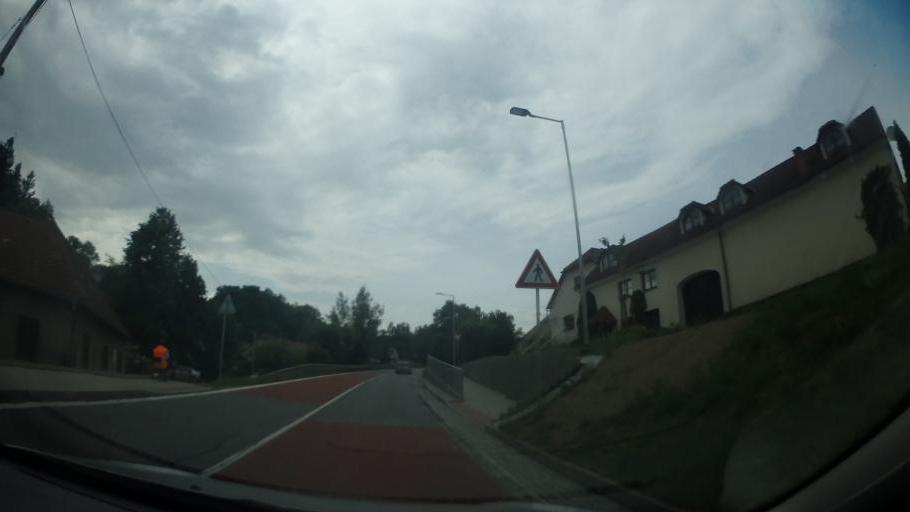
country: CZ
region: Vysocina
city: Bystrice nad Pernstejnem
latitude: 49.5188
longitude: 16.3060
